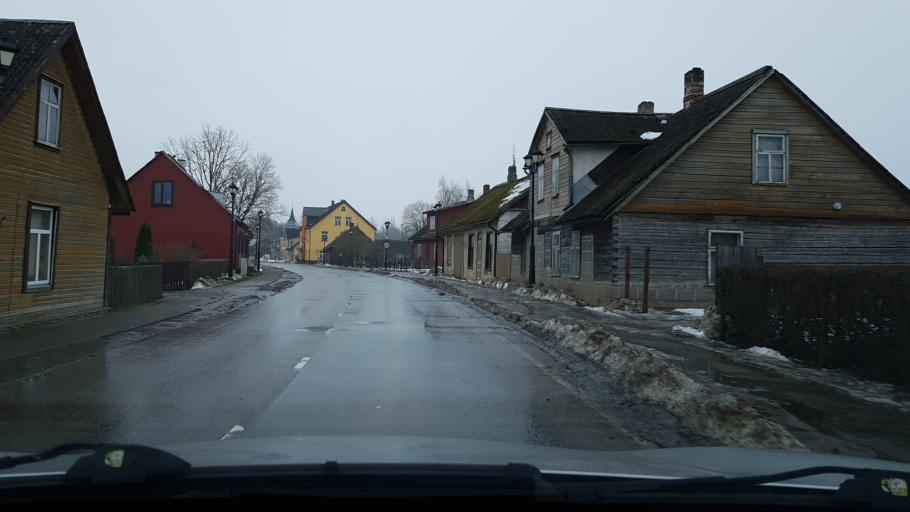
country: EE
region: Valgamaa
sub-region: Torva linn
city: Torva
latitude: 58.2377
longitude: 25.8589
